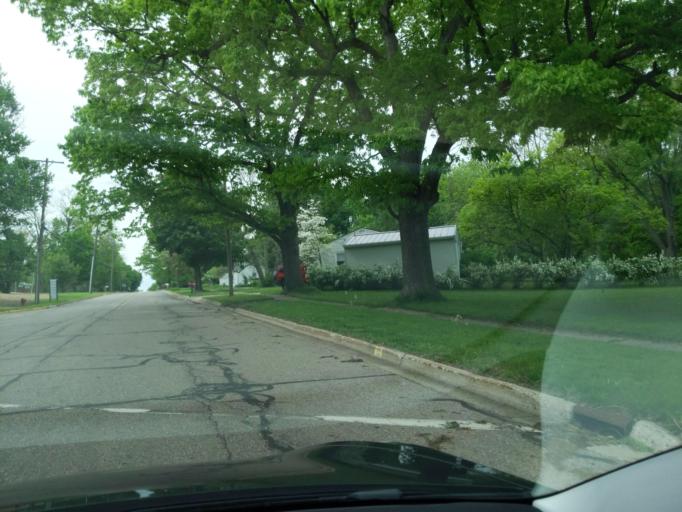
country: US
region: Michigan
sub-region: Ingham County
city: Leslie
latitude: 42.4566
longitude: -84.4331
